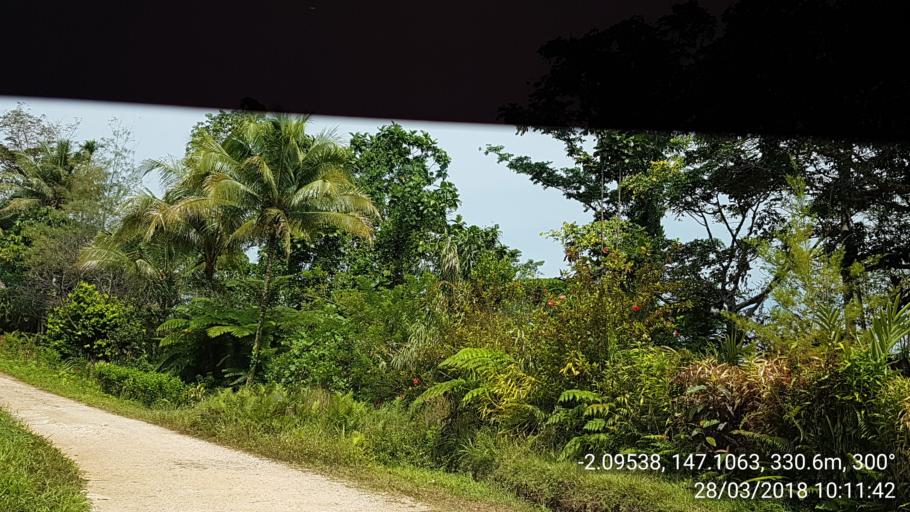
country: PG
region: Manus
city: Lorengau
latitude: -2.0953
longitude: 147.1064
